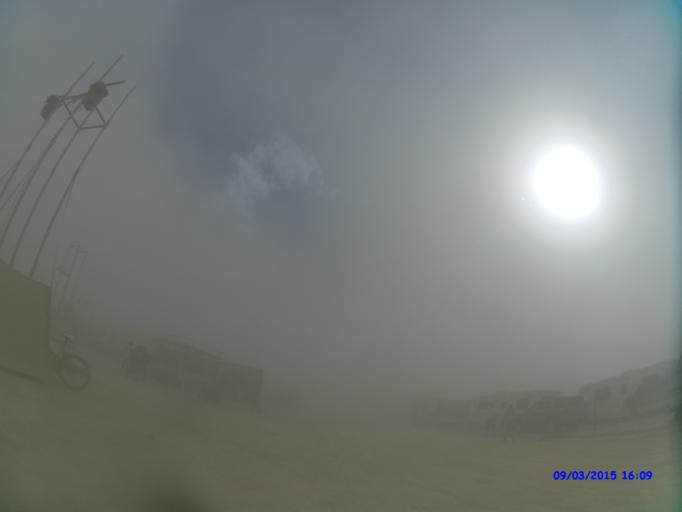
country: US
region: Nevada
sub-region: Pershing County
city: Lovelock
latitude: 40.7842
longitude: -119.1962
